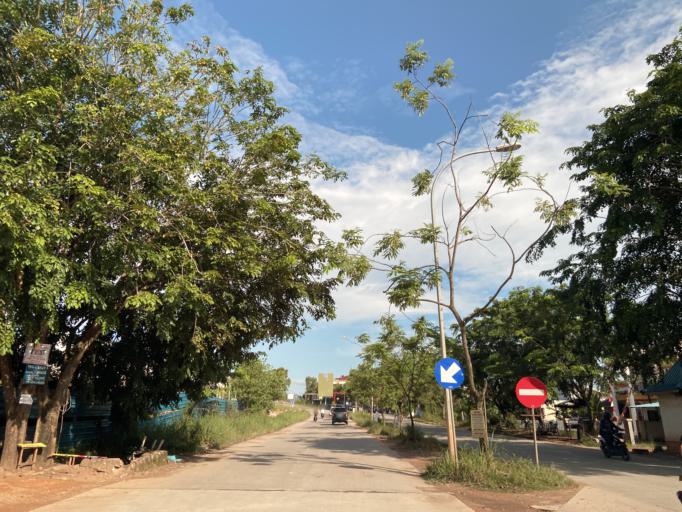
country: SG
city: Singapore
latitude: 1.1096
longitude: 104.0786
